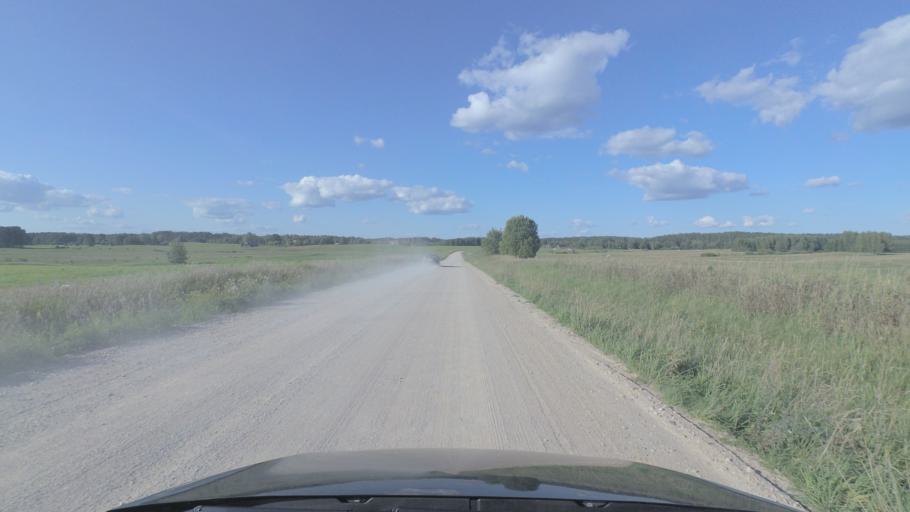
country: LT
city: Pabrade
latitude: 55.1319
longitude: 25.7065
